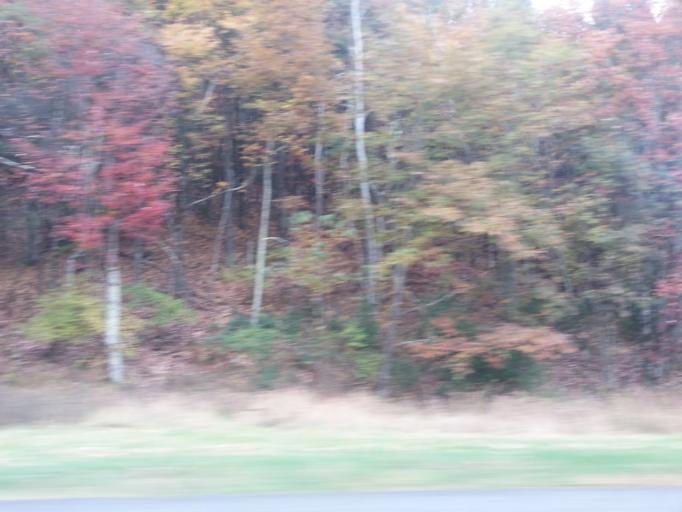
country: US
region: North Carolina
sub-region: Ashe County
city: Jefferson
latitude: 36.2868
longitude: -81.3739
